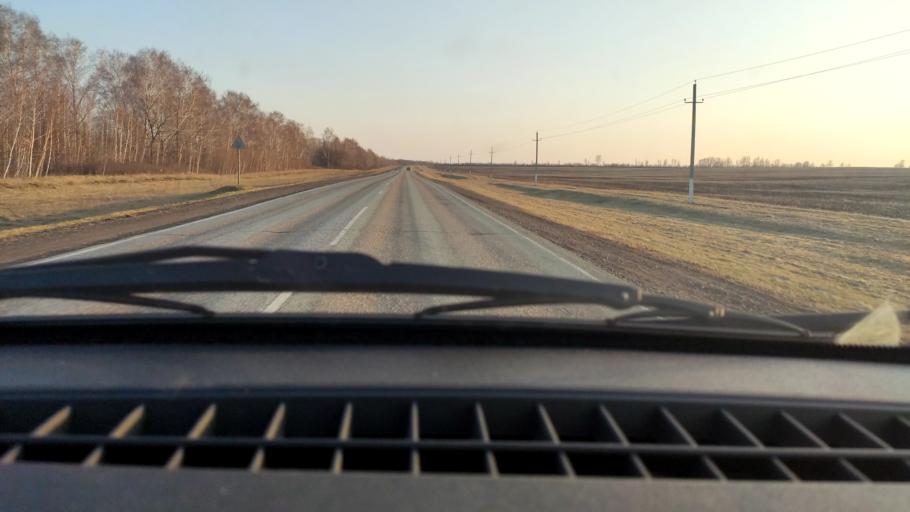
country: RU
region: Bashkortostan
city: Davlekanovo
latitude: 54.3399
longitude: 55.1719
